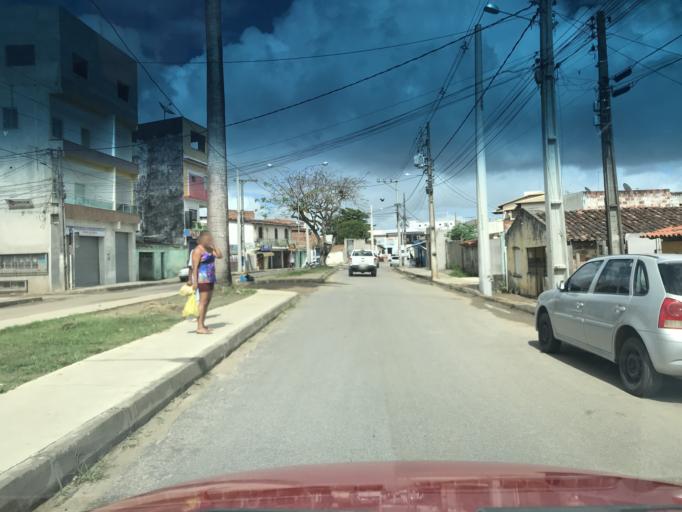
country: BR
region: Bahia
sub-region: Santo Antonio De Jesus
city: Santo Antonio de Jesus
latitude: -12.9781
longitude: -39.2756
